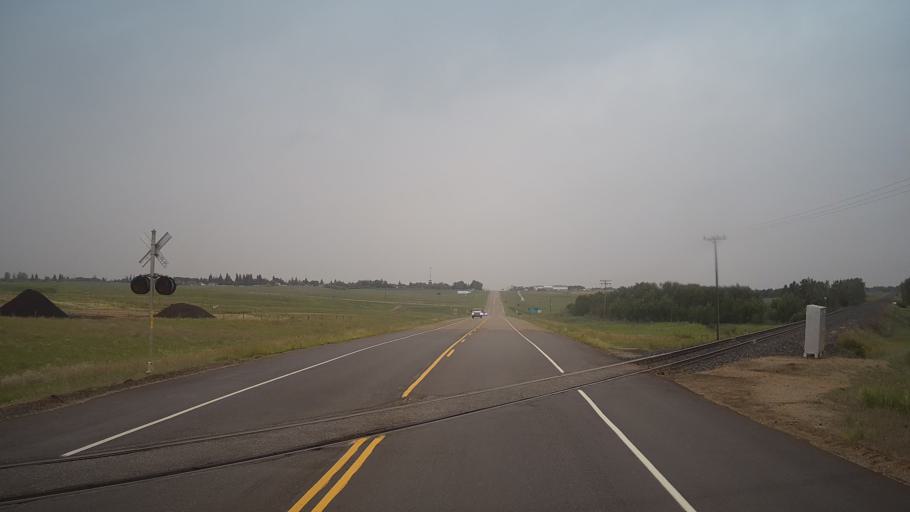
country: CA
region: Saskatchewan
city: Biggar
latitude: 52.0577
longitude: -107.9558
